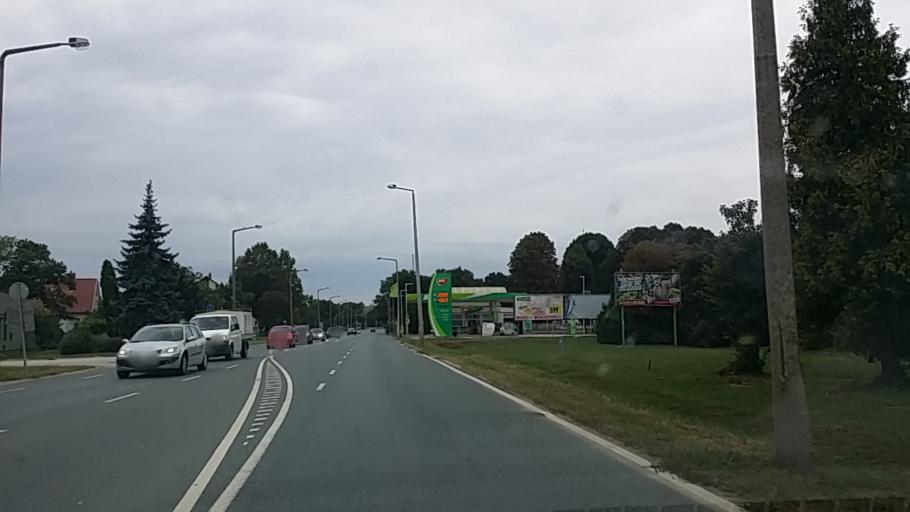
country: HU
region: Gyor-Moson-Sopron
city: Kapuvar
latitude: 47.5920
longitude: 17.0341
